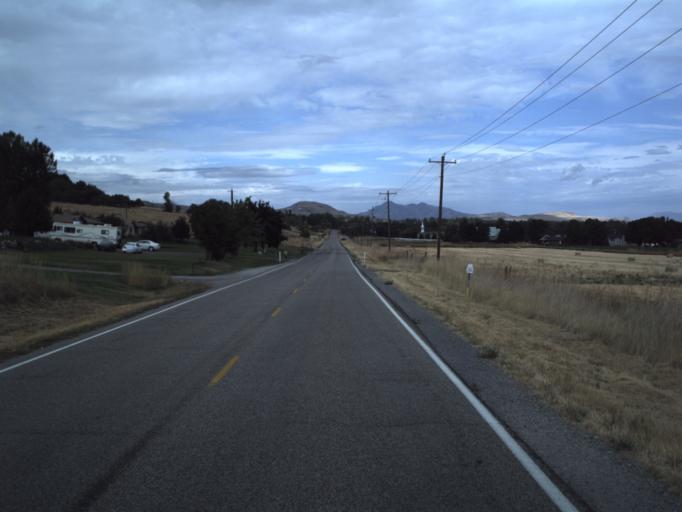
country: US
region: Utah
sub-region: Cache County
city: Mendon
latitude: 41.6906
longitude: -111.9692
